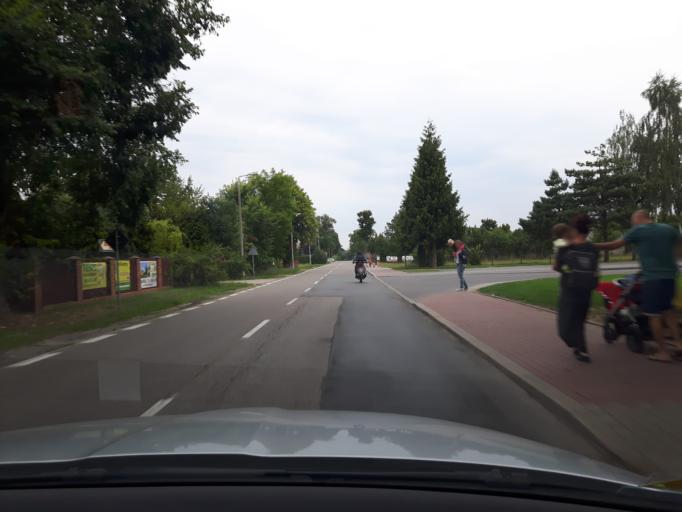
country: PL
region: Masovian Voivodeship
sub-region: Powiat legionowski
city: Wieliszew
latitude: 52.4862
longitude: 20.9703
